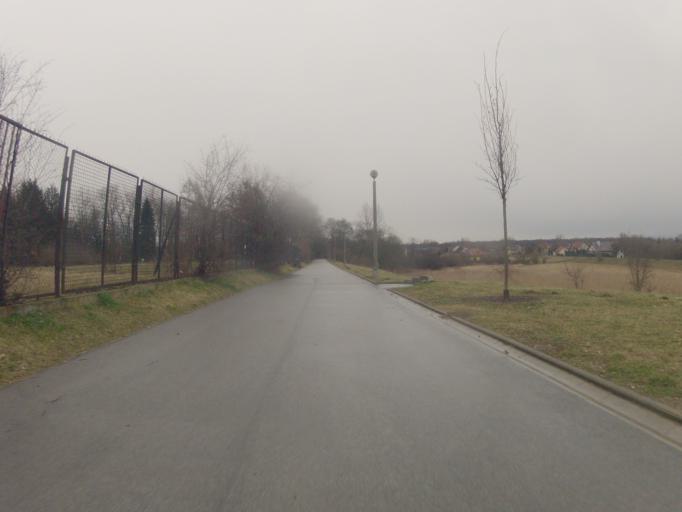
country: PL
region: Lesser Poland Voivodeship
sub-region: Powiat wielicki
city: Kokotow
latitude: 50.0643
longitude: 20.0447
